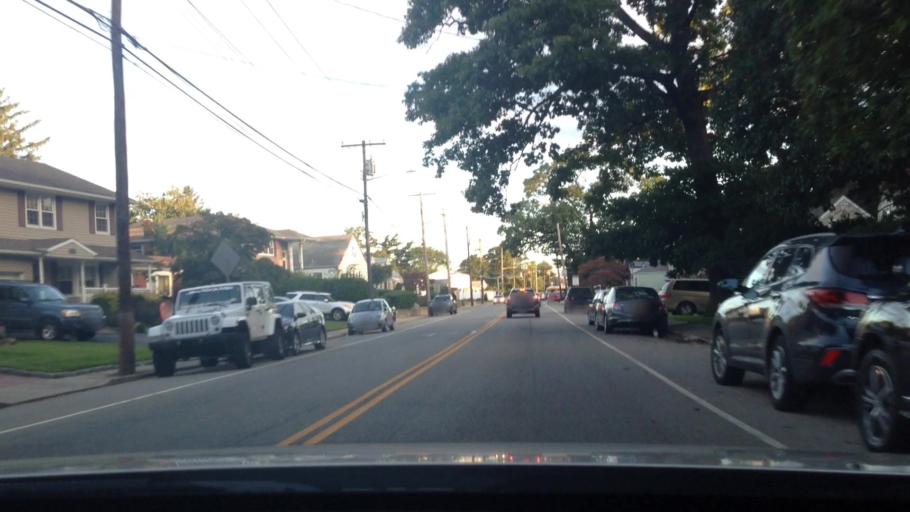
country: US
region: New York
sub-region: Nassau County
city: West Hempstead
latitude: 40.6975
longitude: -73.6602
